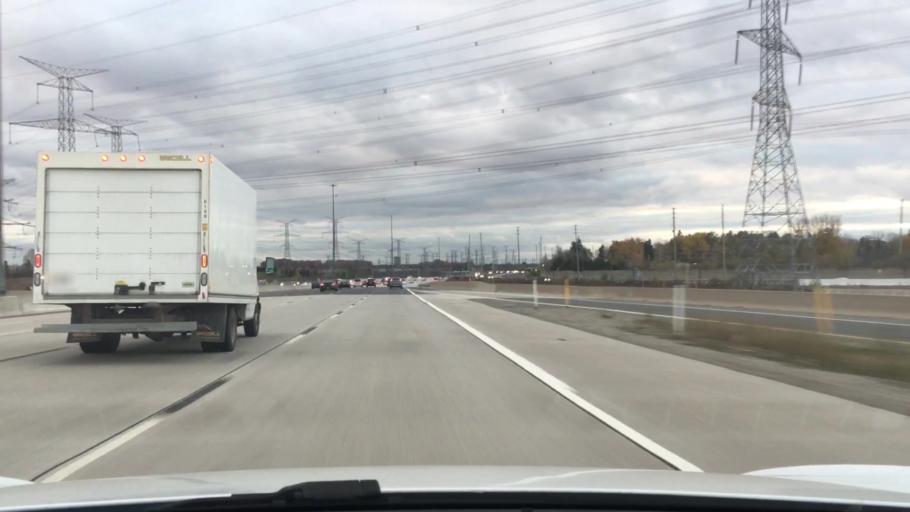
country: CA
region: Ontario
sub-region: York
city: Richmond Hill
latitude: 43.8352
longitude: -79.4271
